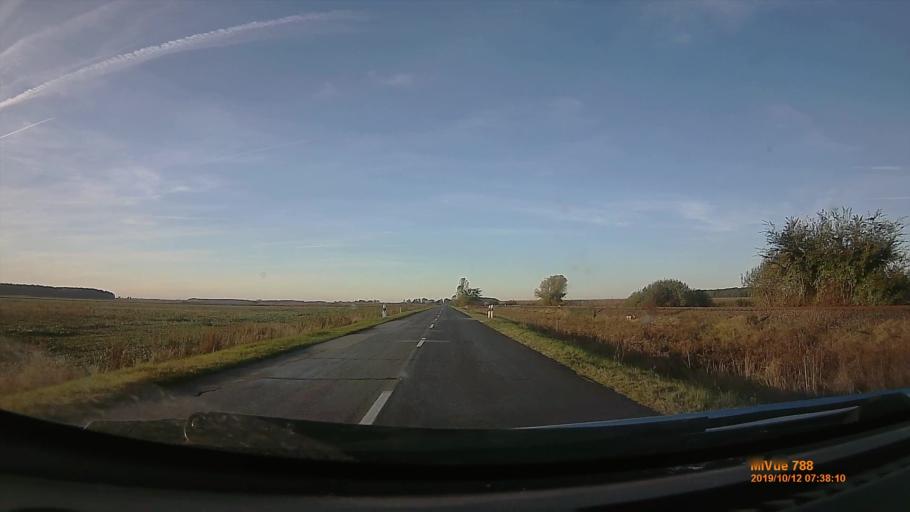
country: HU
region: Hajdu-Bihar
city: Pocsaj
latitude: 47.2279
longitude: 21.8117
